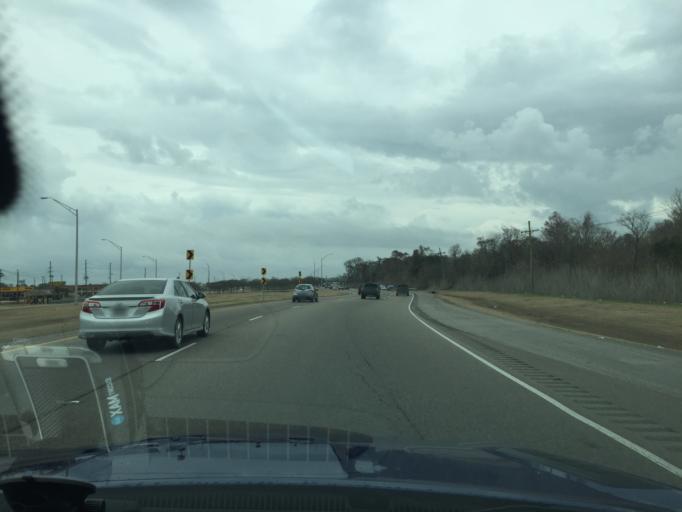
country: US
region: Louisiana
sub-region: Jefferson Parish
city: Westwego
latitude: 29.9058
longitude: -90.1586
